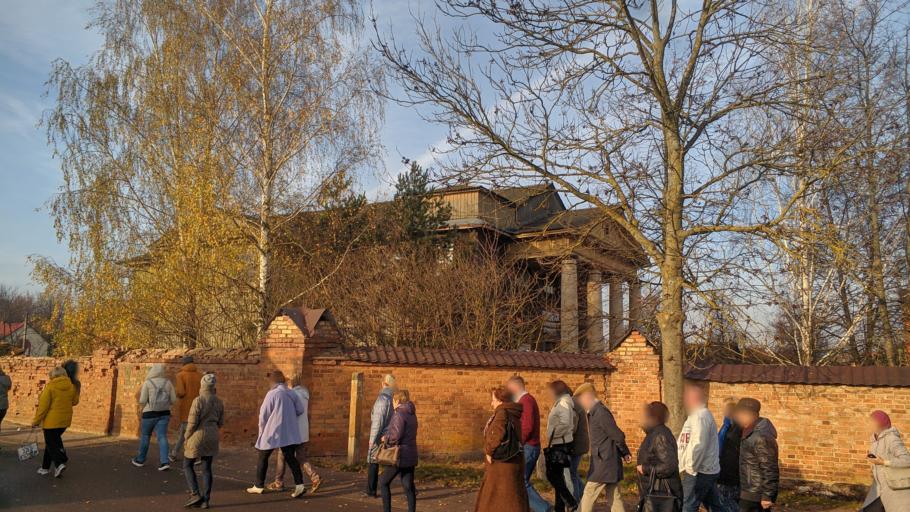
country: BY
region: Minsk
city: Uzda
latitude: 53.4575
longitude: 27.2176
